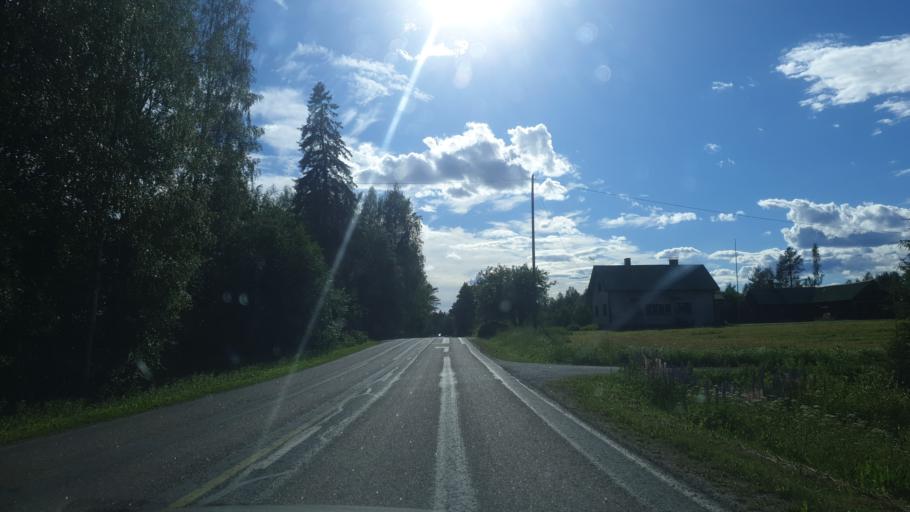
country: FI
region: Southern Savonia
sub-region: Mikkeli
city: Pertunmaa
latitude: 61.5245
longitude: 26.5349
